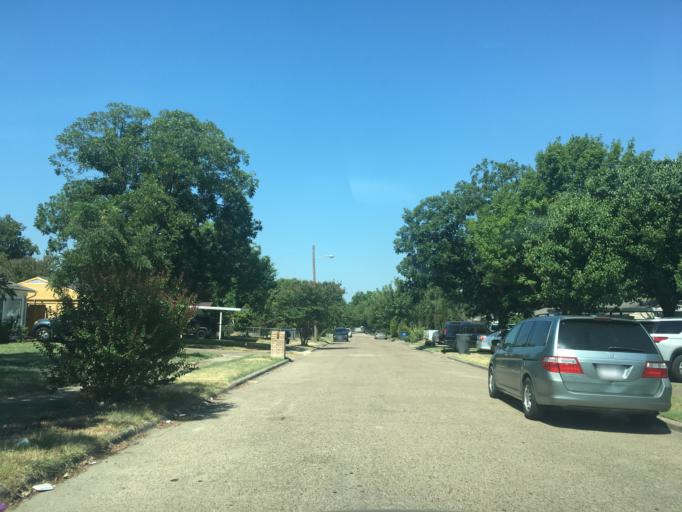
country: US
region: Texas
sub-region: Dallas County
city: Garland
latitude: 32.8550
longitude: -96.6713
